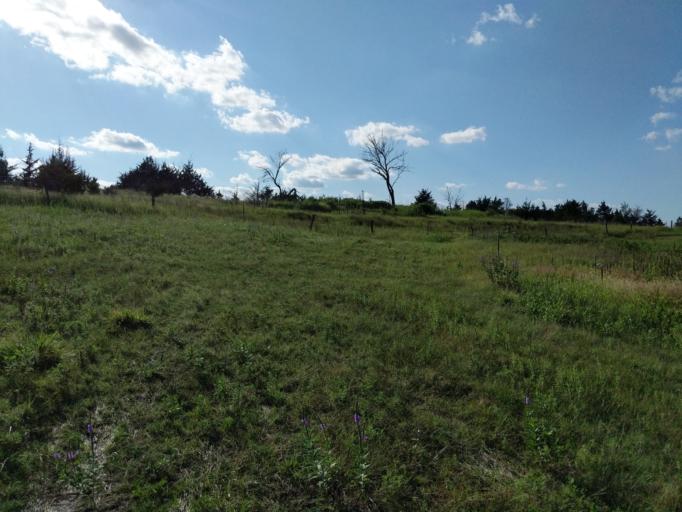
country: US
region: Kansas
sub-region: Smith County
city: Smith Center
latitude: 39.8899
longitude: -98.9495
